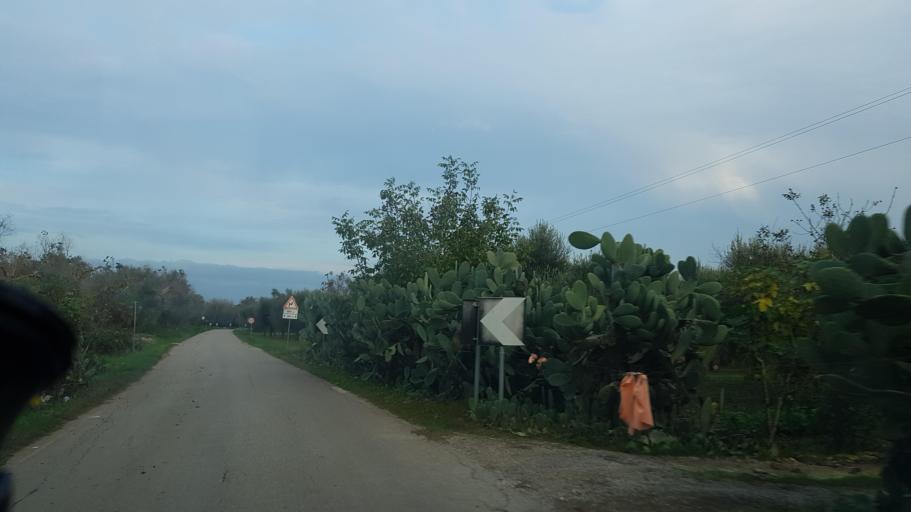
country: IT
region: Apulia
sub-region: Provincia di Brindisi
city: Latiano
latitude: 40.5380
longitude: 17.7506
